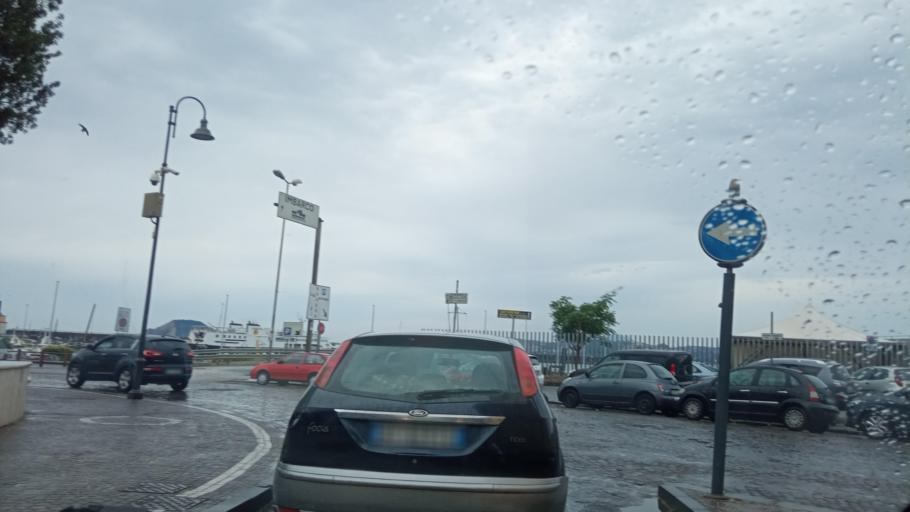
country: IT
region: Campania
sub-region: Provincia di Napoli
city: Pozzuoli
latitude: 40.8263
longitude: 14.1197
